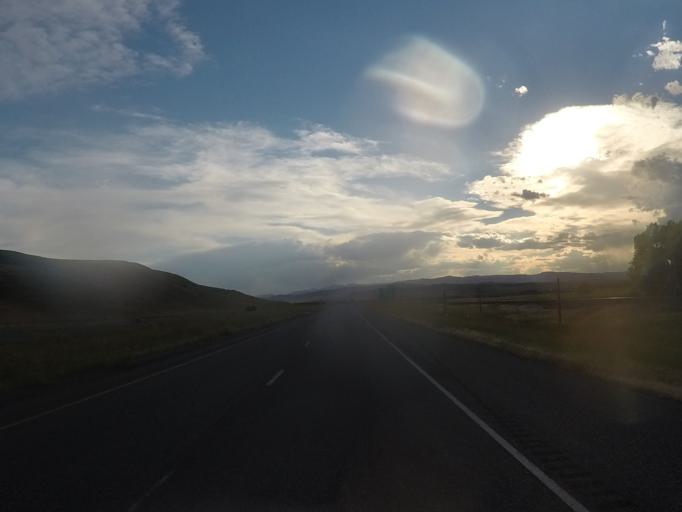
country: US
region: Montana
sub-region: Park County
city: Livingston
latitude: 45.7130
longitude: -110.4291
